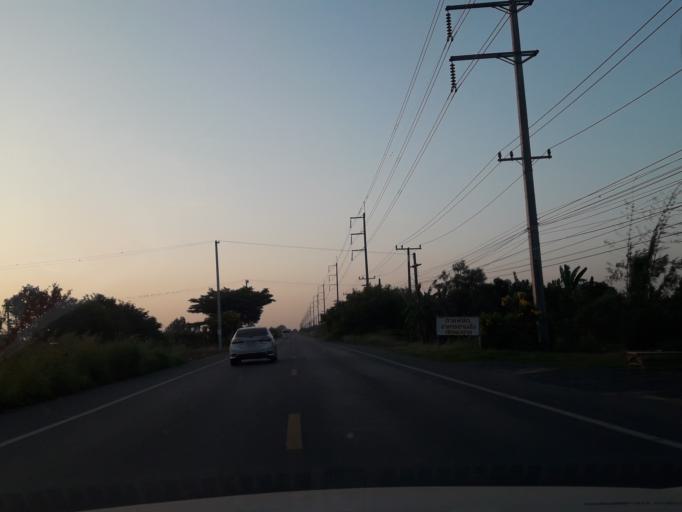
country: TH
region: Phra Nakhon Si Ayutthaya
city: Maha Rat
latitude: 14.5061
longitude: 100.5493
